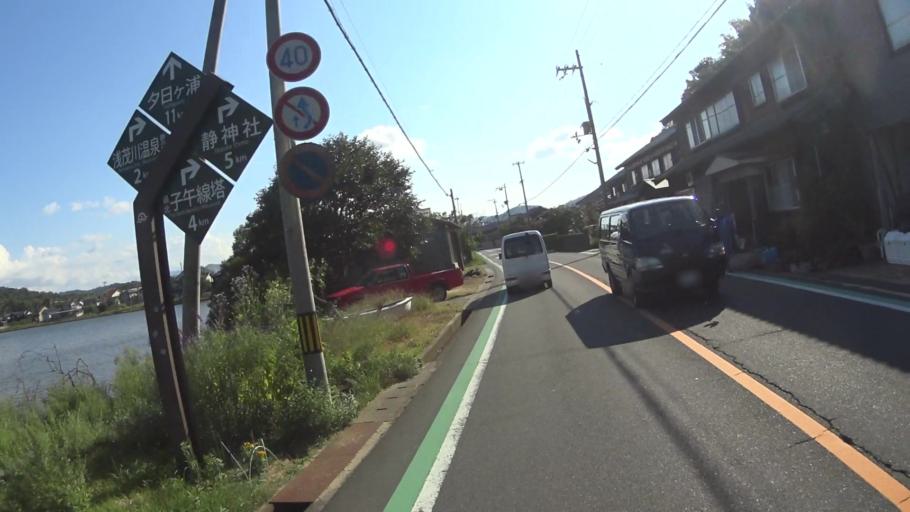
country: JP
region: Kyoto
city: Miyazu
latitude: 35.6927
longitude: 135.0361
